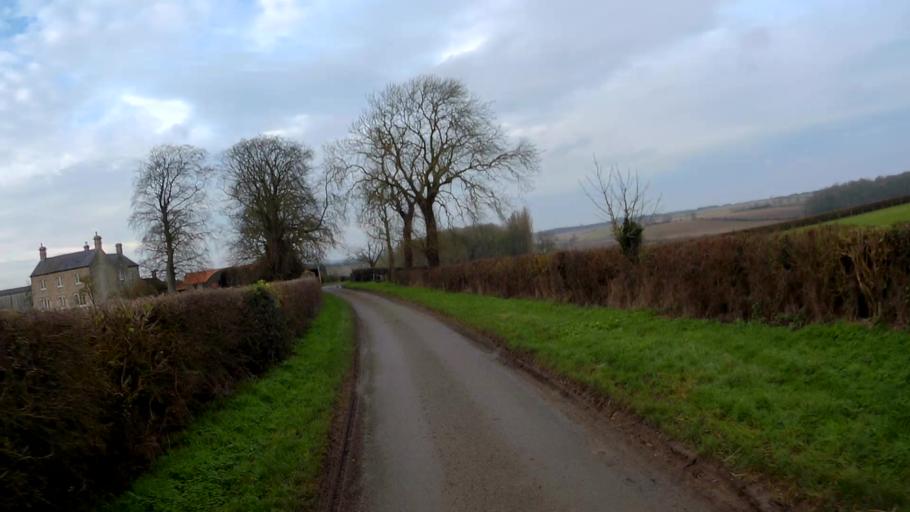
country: GB
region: England
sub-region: Lincolnshire
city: Bourne
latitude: 52.8234
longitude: -0.4586
